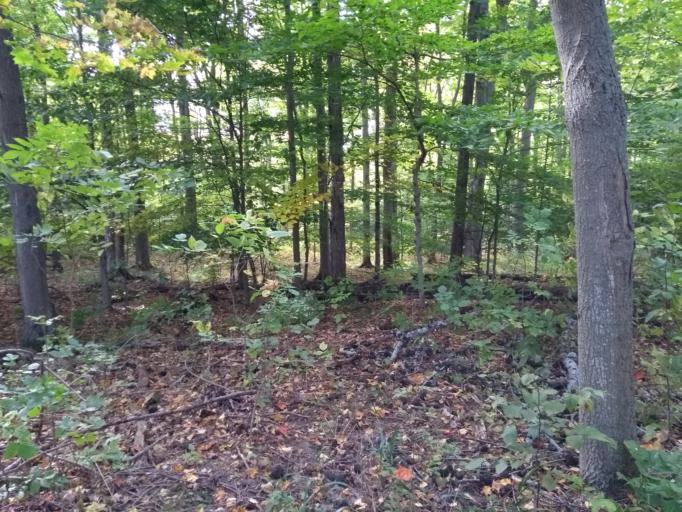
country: CA
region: Ontario
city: Thorold
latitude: 43.0988
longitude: -79.2767
